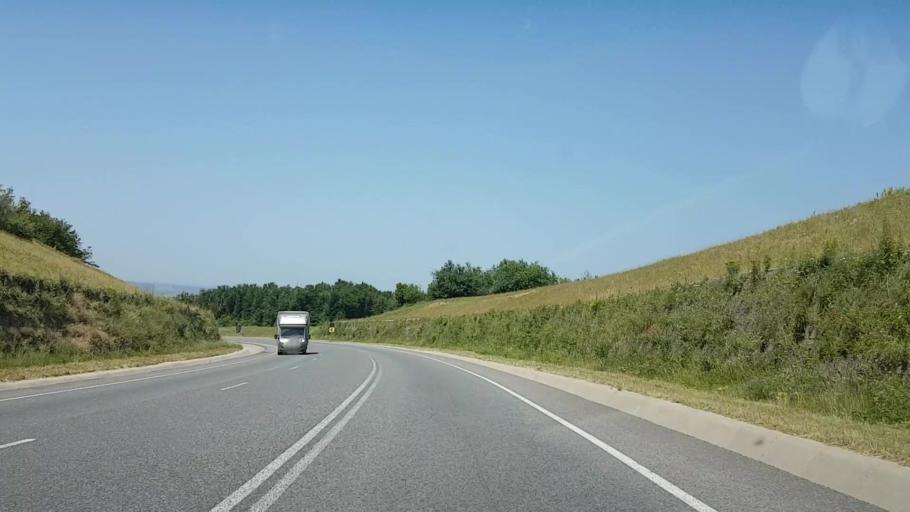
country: RO
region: Cluj
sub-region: Comuna Feleacu
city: Gheorghieni
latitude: 46.7142
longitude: 23.6626
